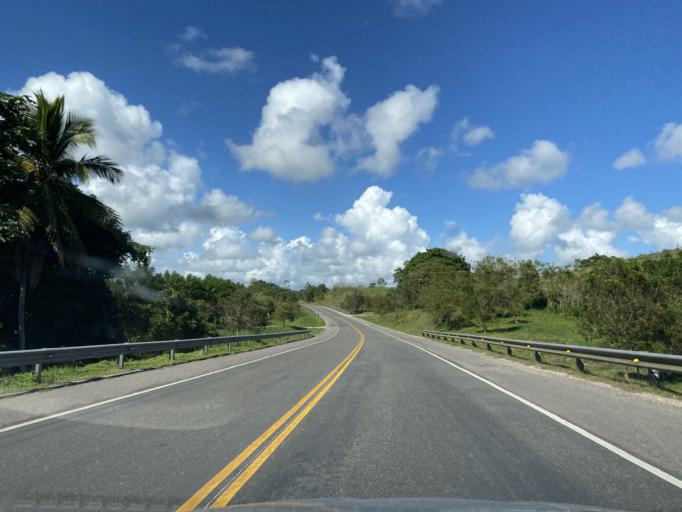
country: DO
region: Monte Plata
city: Majagual
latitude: 19.0236
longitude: -69.8226
